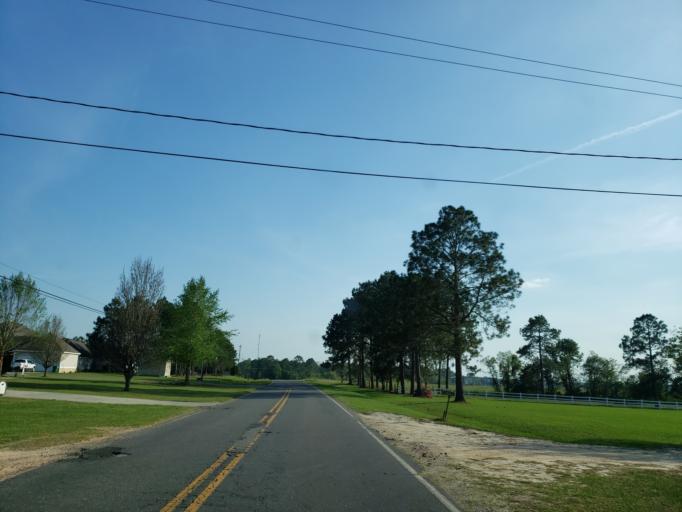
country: US
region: Georgia
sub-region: Tift County
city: Tifton
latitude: 31.4886
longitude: -83.5431
